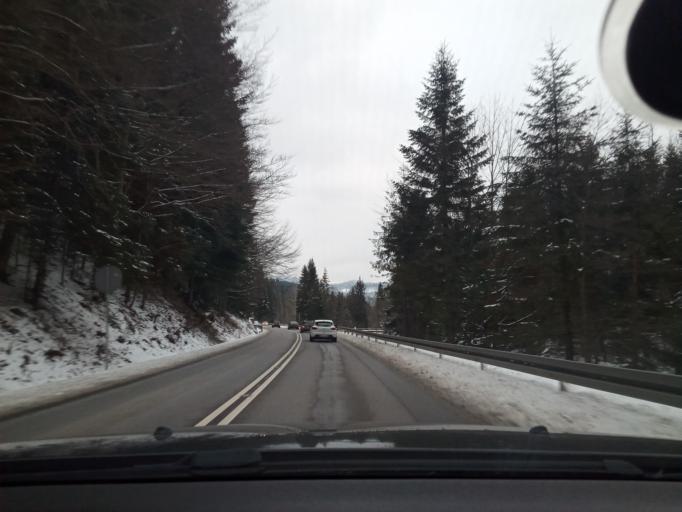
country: PL
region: Lesser Poland Voivodeship
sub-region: Powiat limanowski
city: Lubomierz
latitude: 49.6130
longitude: 20.2375
